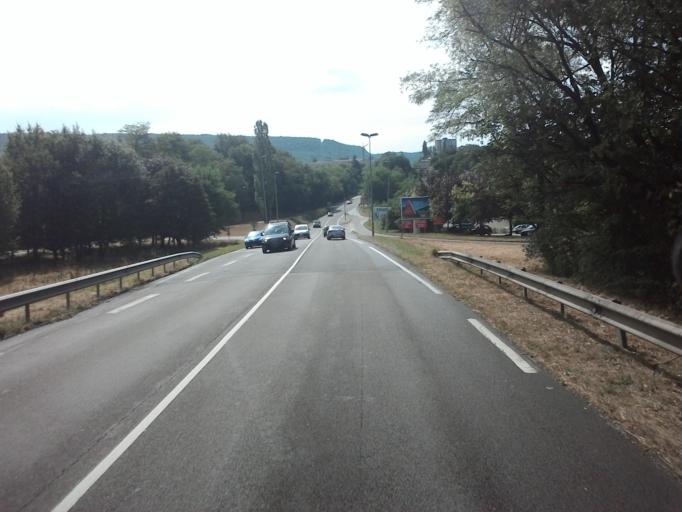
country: FR
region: Franche-Comte
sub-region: Departement du Jura
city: Lons-le-Saunier
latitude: 46.6875
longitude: 5.5630
